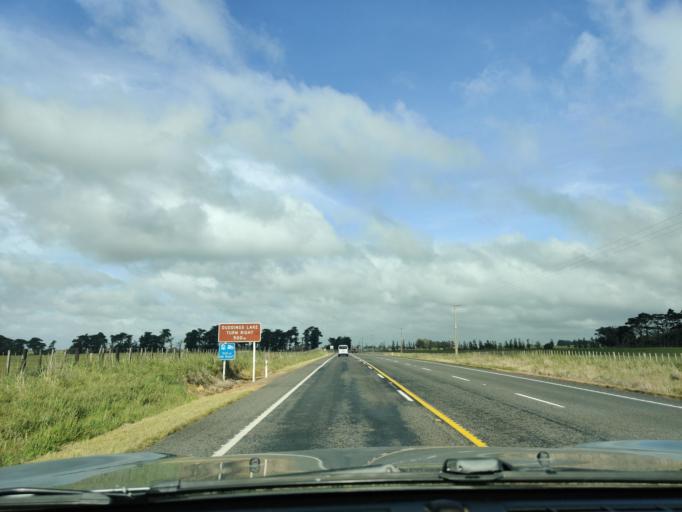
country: NZ
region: Manawatu-Wanganui
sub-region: Rangitikei District
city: Bulls
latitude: -40.0923
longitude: 175.2784
